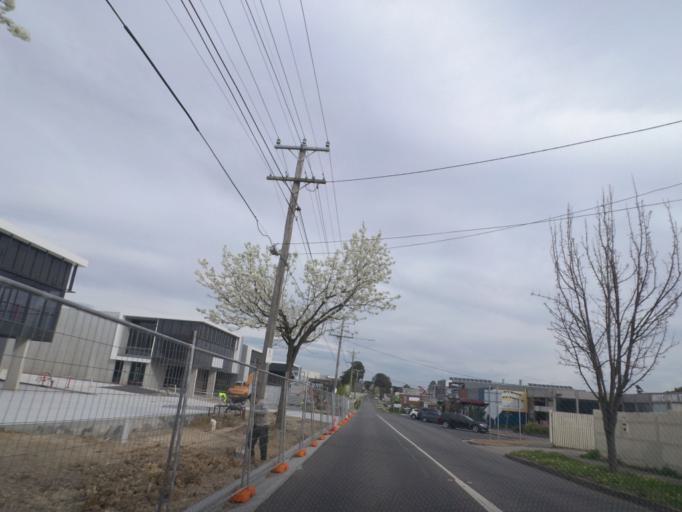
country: AU
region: Victoria
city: Forest Hill
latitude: -37.8297
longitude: 145.1869
